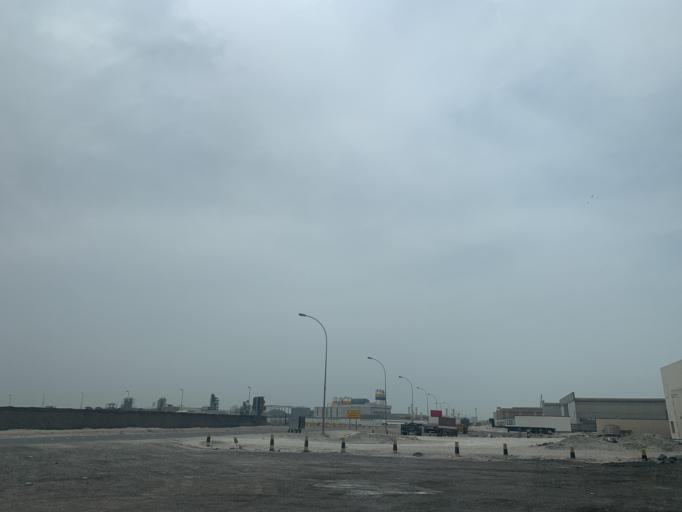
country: BH
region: Muharraq
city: Al Hadd
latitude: 26.2044
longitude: 50.6779
